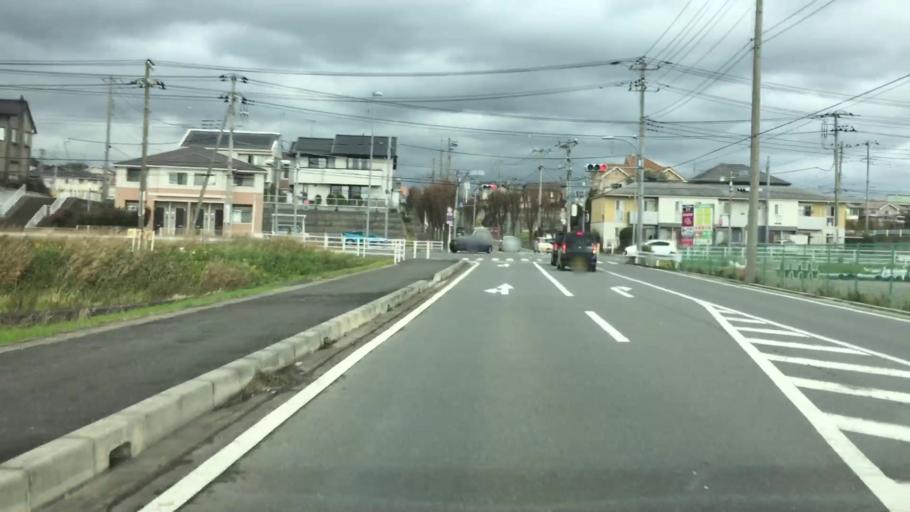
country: JP
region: Ibaraki
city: Toride
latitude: 35.8581
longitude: 140.1035
